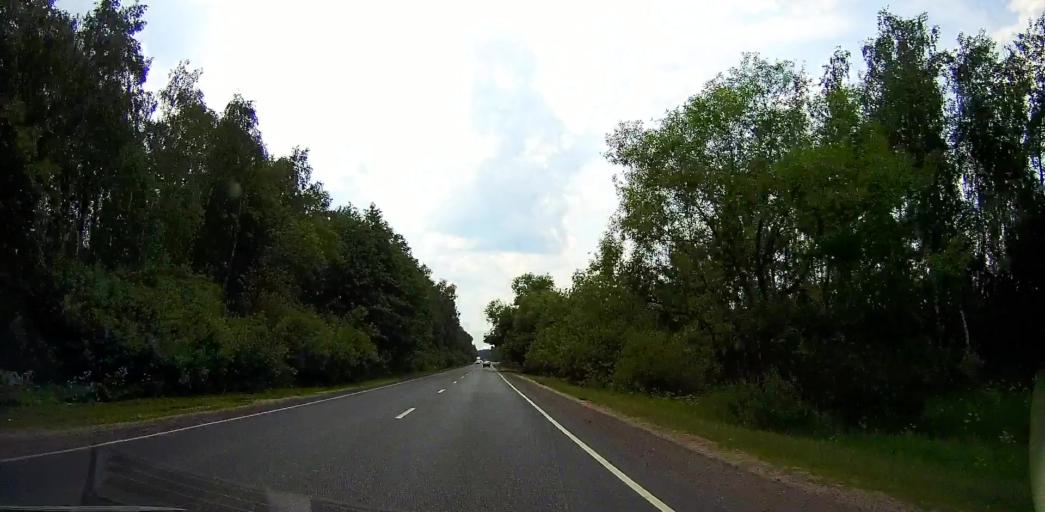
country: RU
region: Moskovskaya
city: Stupino
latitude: 54.9341
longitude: 38.1294
